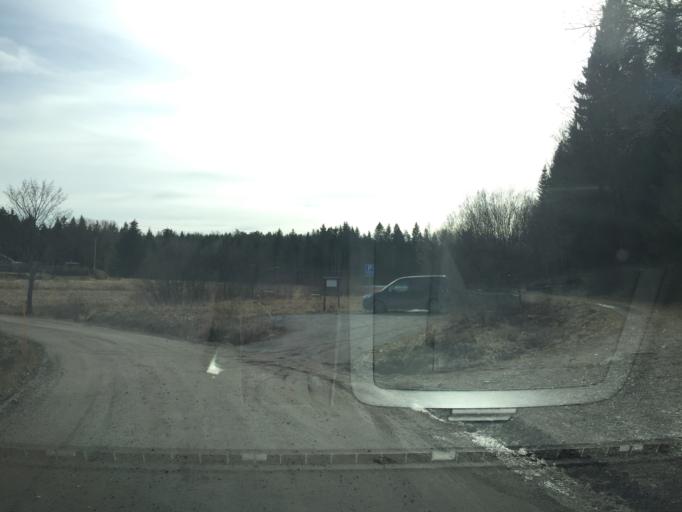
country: SE
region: Stockholm
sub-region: Botkyrka Kommun
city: Tullinge
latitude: 59.0983
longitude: 17.9682
